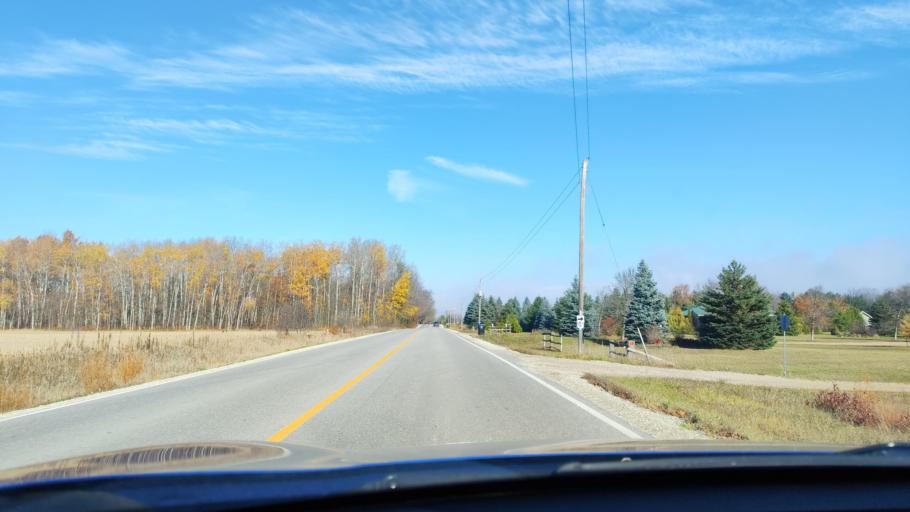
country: CA
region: Ontario
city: Wasaga Beach
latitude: 44.4093
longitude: -80.0599
